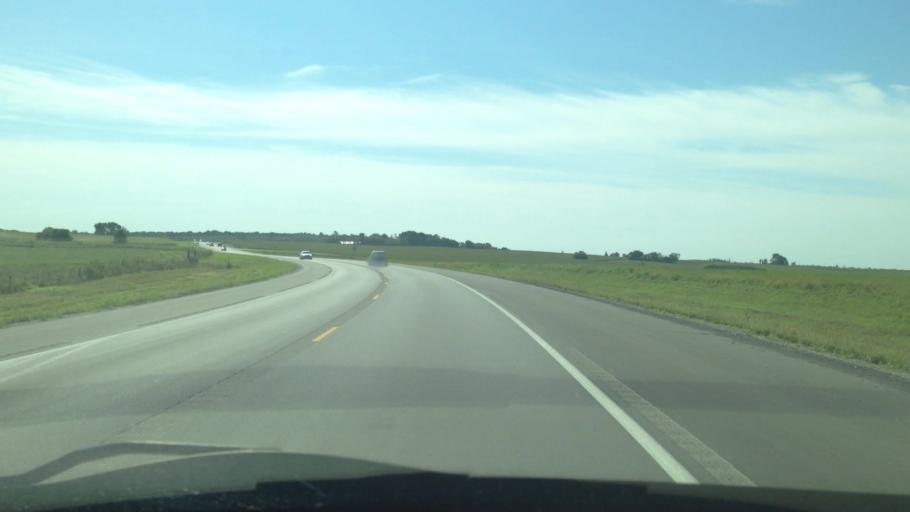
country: US
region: Minnesota
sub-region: Fillmore County
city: Harmony
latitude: 43.6157
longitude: -92.0193
